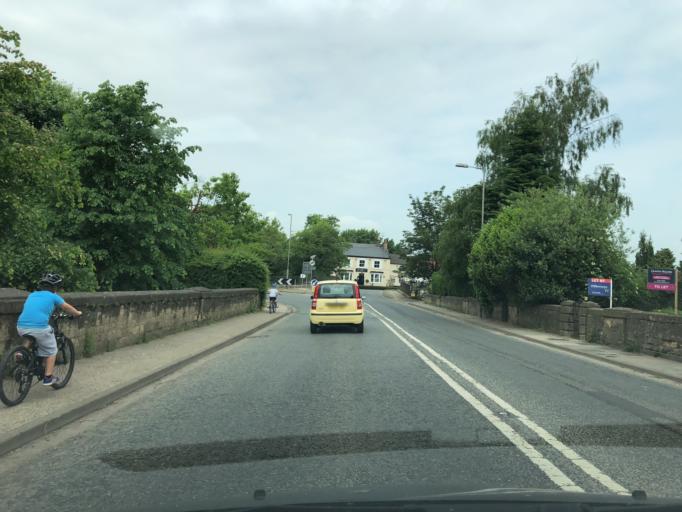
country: GB
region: England
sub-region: North Yorkshire
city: Boroughbridge
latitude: 54.0979
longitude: -1.3957
